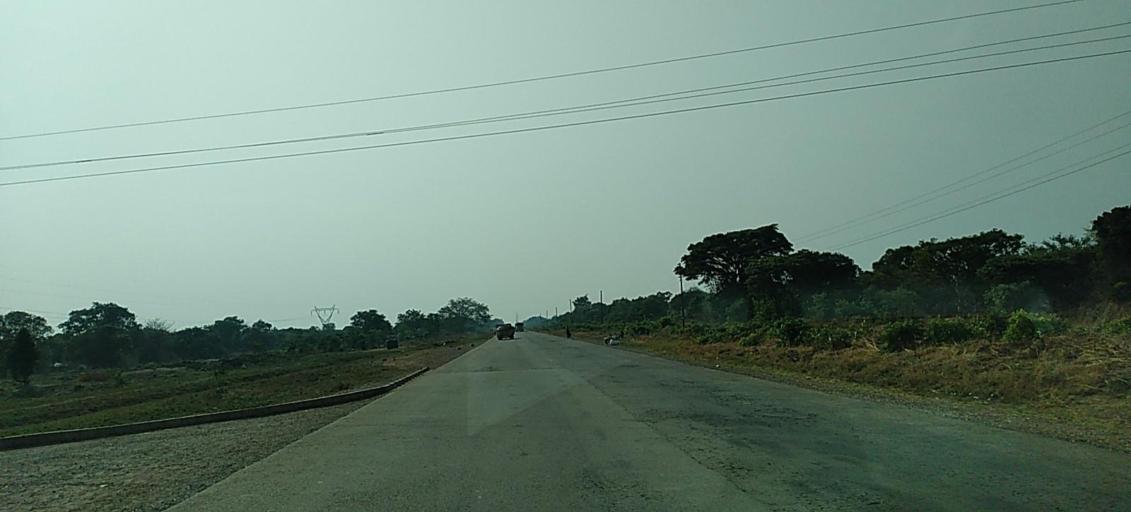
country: ZM
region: North-Western
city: Kansanshi
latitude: -12.3027
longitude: 26.9868
